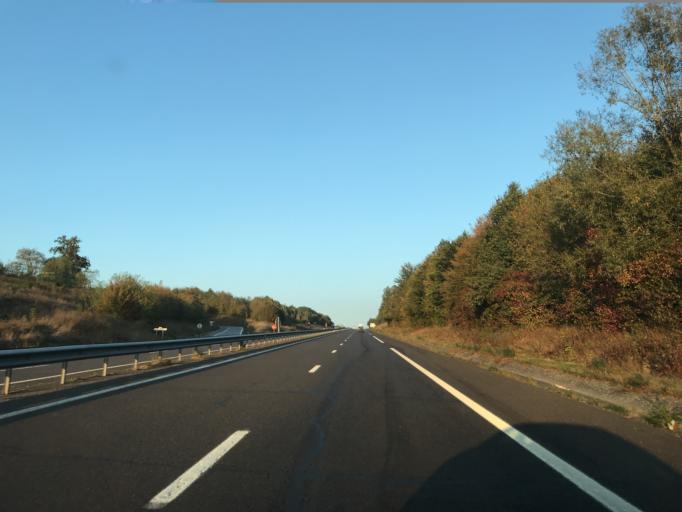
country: FR
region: Lower Normandy
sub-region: Departement de l'Orne
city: Mortagne-au-Perche
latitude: 48.5218
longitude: 0.4876
